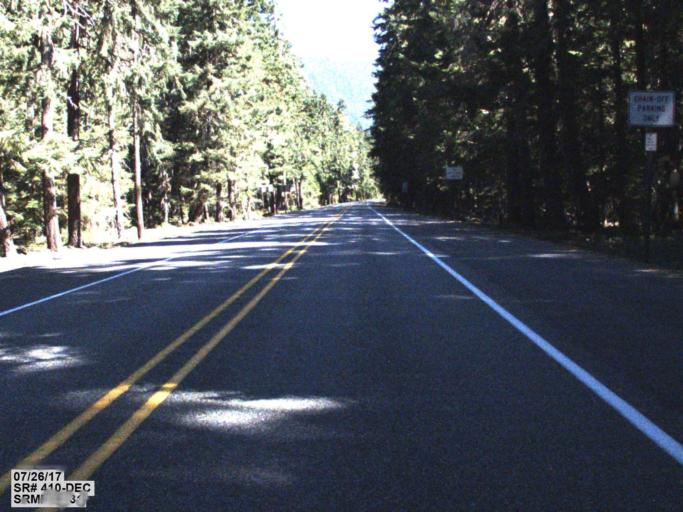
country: US
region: Washington
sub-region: King County
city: Enumclaw
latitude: 46.9825
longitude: -121.5356
